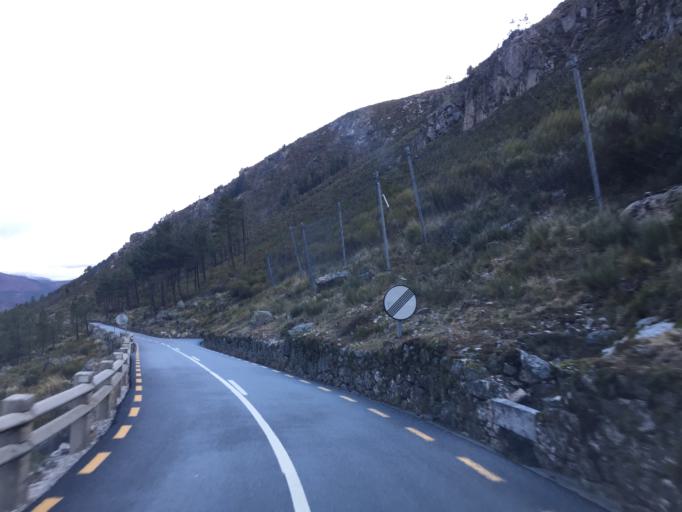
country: PT
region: Guarda
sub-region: Manteigas
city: Manteigas
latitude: 40.3555
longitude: -7.5575
